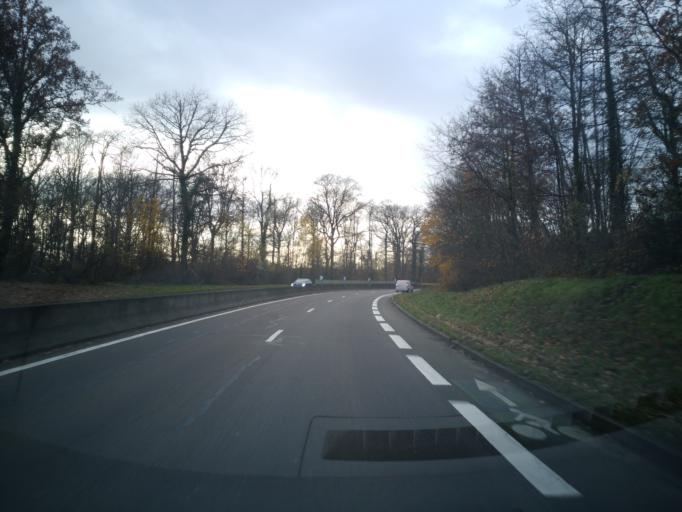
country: FR
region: Ile-de-France
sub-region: Departement des Yvelines
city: Buc
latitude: 48.7794
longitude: 2.1034
